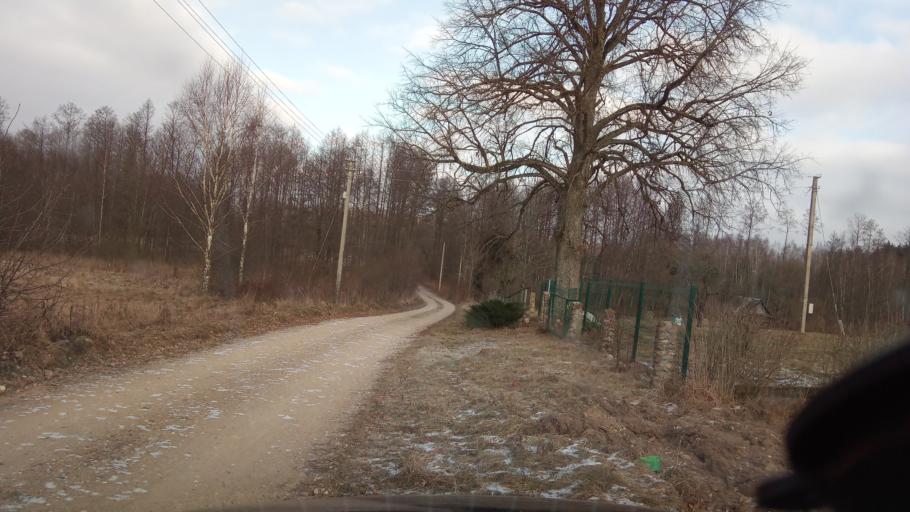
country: LT
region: Alytaus apskritis
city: Varena
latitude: 54.1303
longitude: 24.6458
